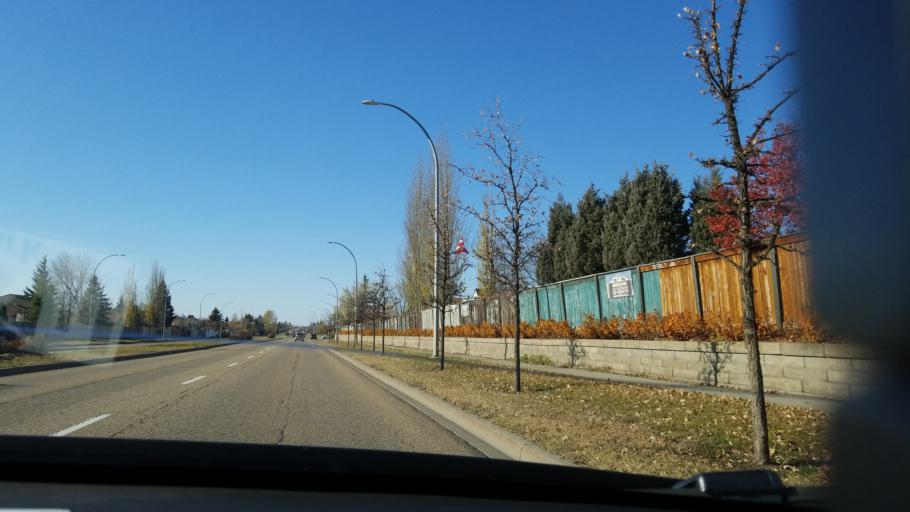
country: CA
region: Alberta
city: Edmonton
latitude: 53.6159
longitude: -113.4510
